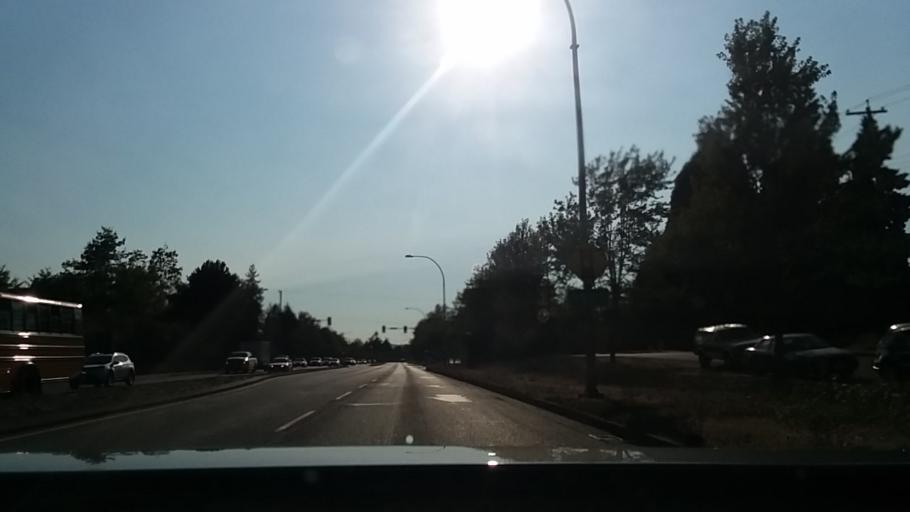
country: CA
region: British Columbia
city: Victoria
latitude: 48.4672
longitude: -123.3862
